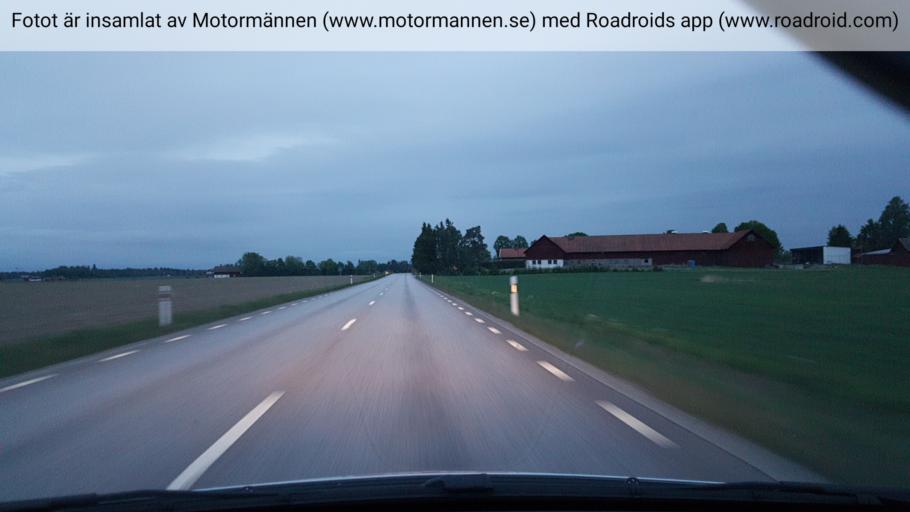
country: SE
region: Vaestmanland
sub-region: Sala Kommun
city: Sala
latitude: 59.8681
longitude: 16.6287
